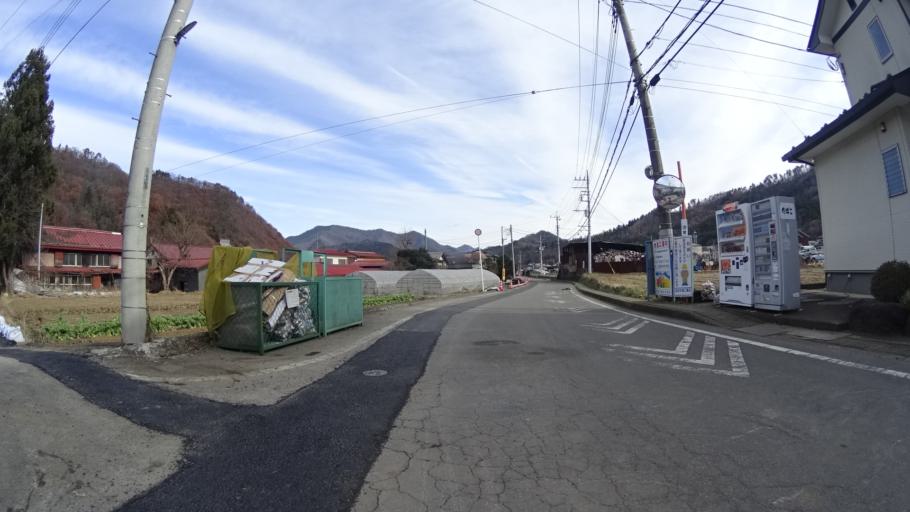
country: JP
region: Yamanashi
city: Otsuki
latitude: 35.5465
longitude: 138.9165
